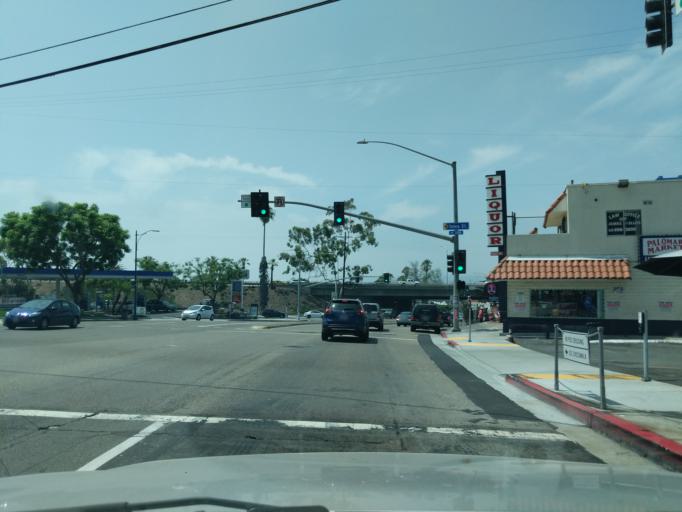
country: US
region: California
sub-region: San Diego County
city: San Diego
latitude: 32.7435
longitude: -117.1812
